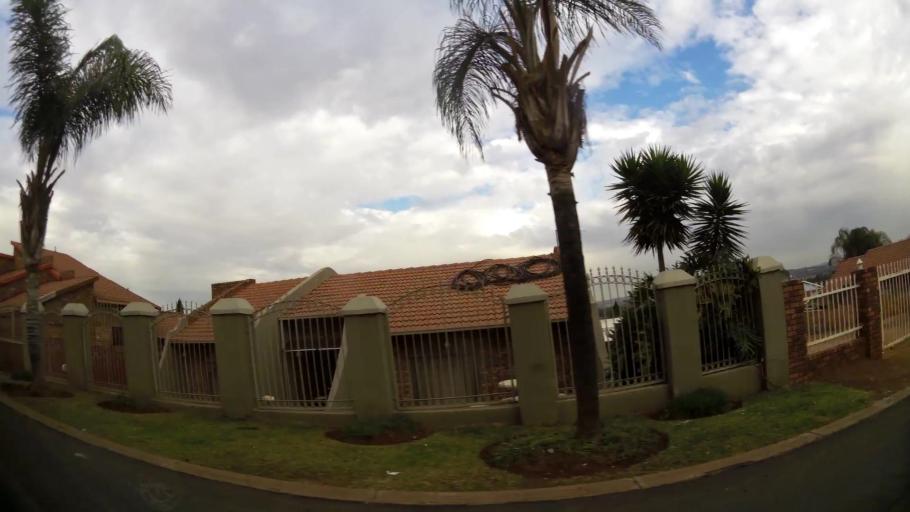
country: ZA
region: Gauteng
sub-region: City of Tshwane Metropolitan Municipality
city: Pretoria
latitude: -25.6976
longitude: 28.3027
